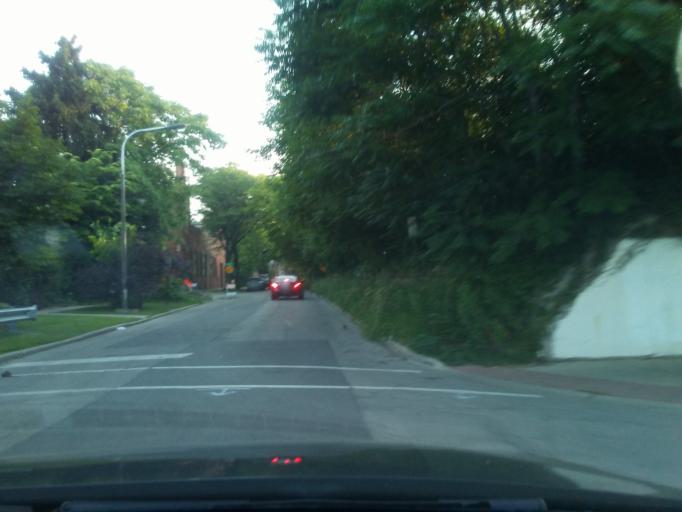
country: US
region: Illinois
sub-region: Cook County
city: Evanston
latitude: 42.0273
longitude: -87.6789
